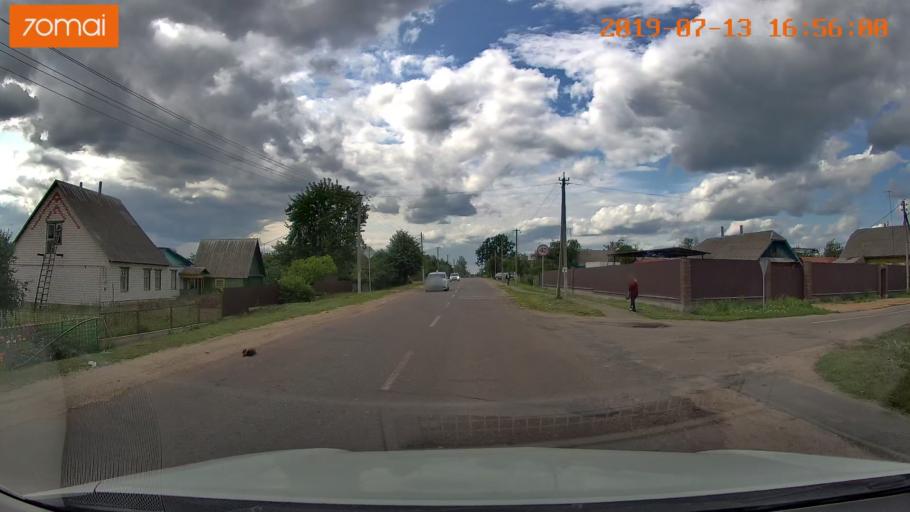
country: BY
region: Mogilev
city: Kirawsk
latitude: 53.2707
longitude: 29.4623
